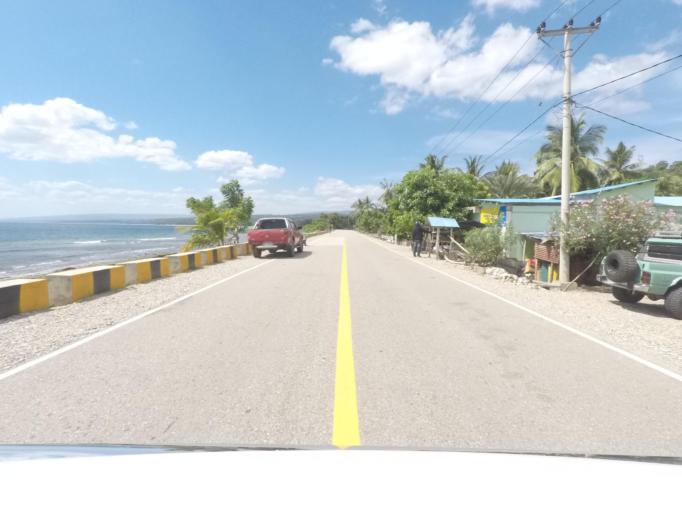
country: TL
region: Lautem
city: Lospalos
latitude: -8.4196
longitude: 126.7547
